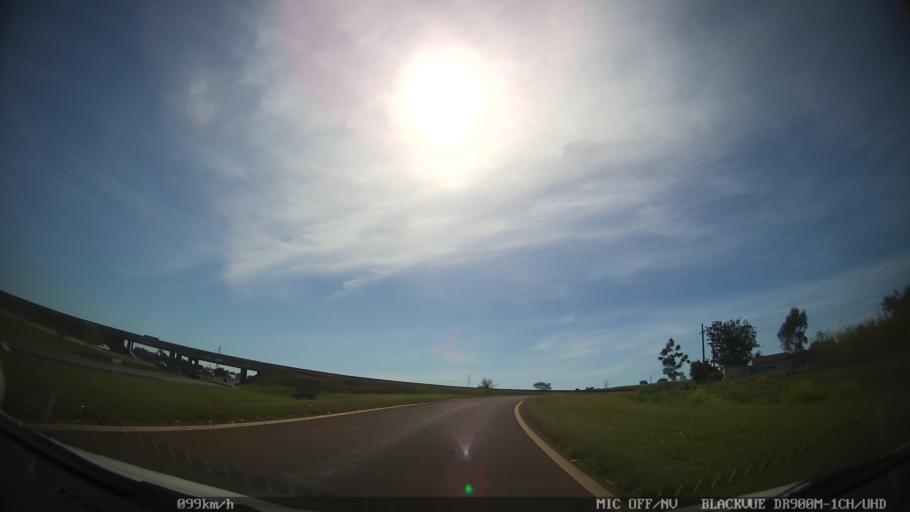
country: BR
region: Sao Paulo
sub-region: Porto Ferreira
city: Porto Ferreira
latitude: -21.8361
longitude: -47.4949
